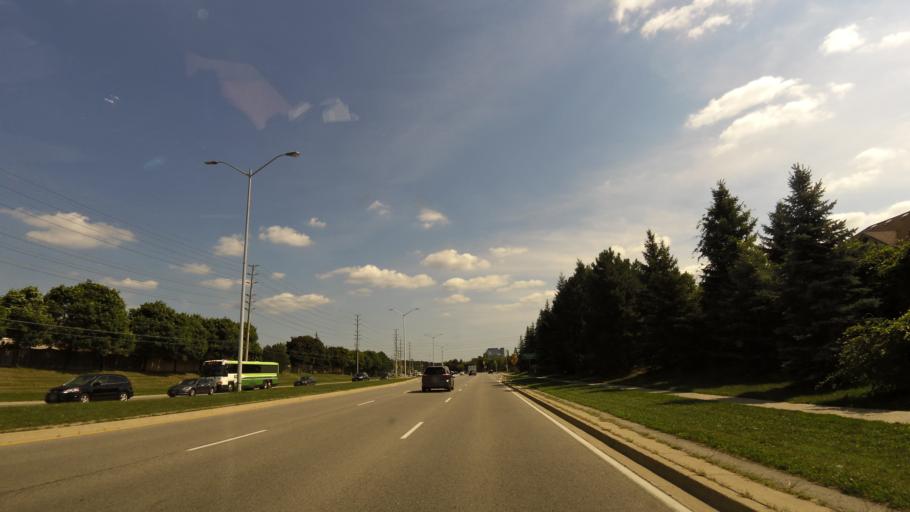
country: CA
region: Ontario
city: Mississauga
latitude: 43.5715
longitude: -79.7254
